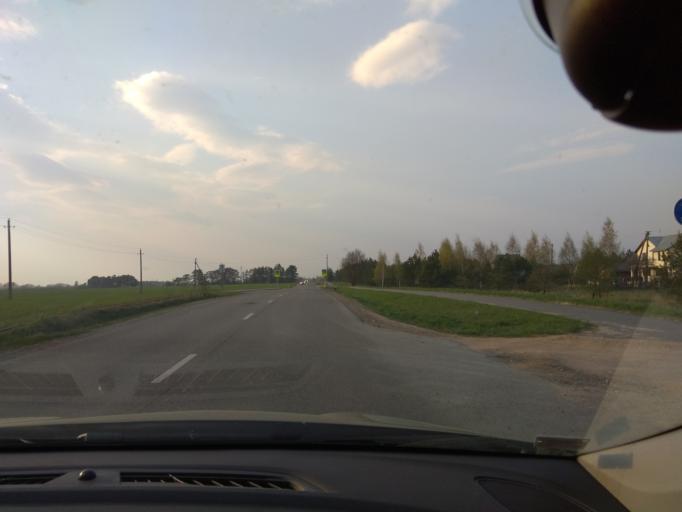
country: LT
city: Grigiskes
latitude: 54.6164
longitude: 25.1174
